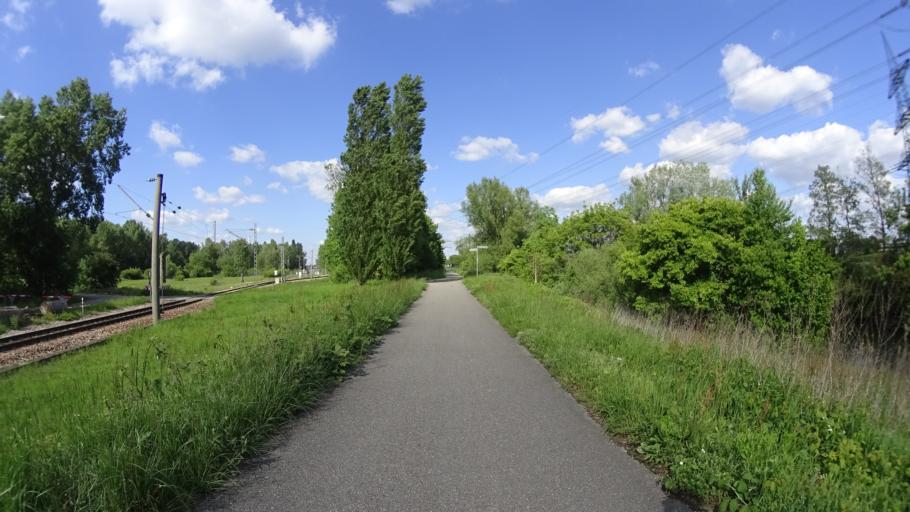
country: DE
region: Rheinland-Pfalz
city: Worth am Rhein
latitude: 49.0440
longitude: 8.3228
